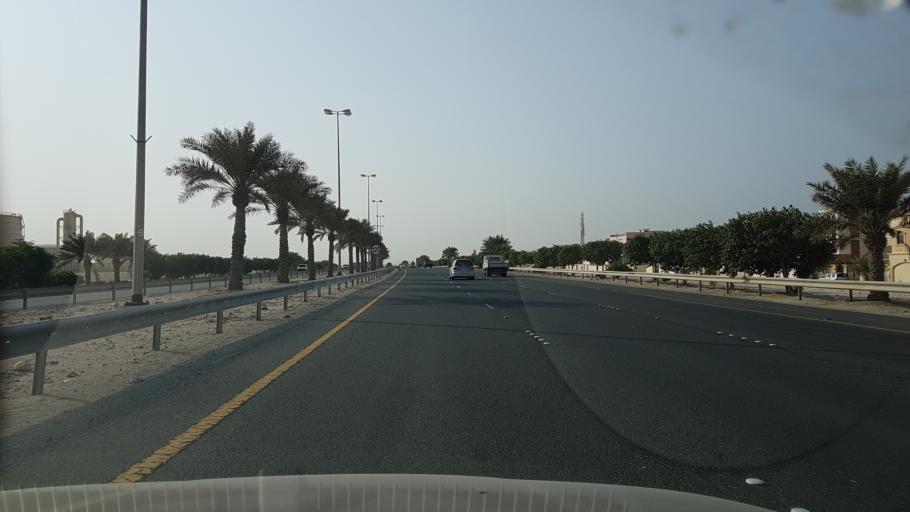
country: BH
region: Central Governorate
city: Dar Kulayb
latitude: 26.0757
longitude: 50.5147
